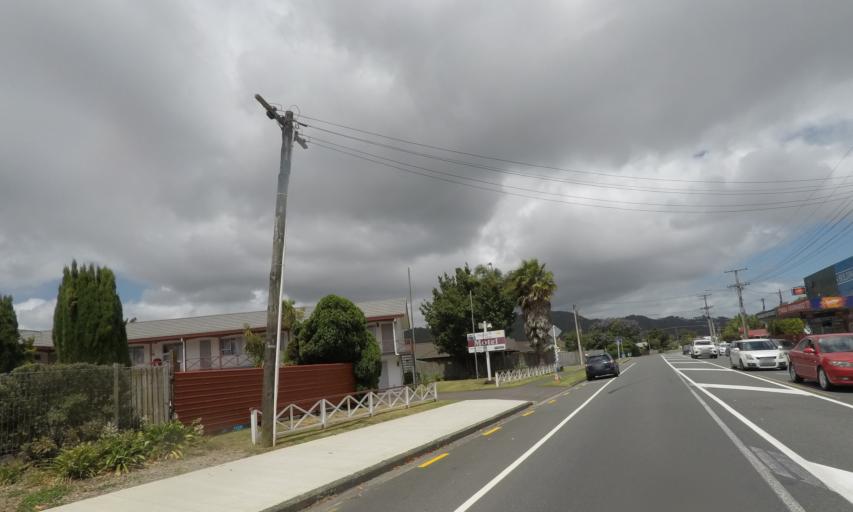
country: NZ
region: Northland
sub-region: Whangarei
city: Whangarei
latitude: -35.7041
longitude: 174.3176
